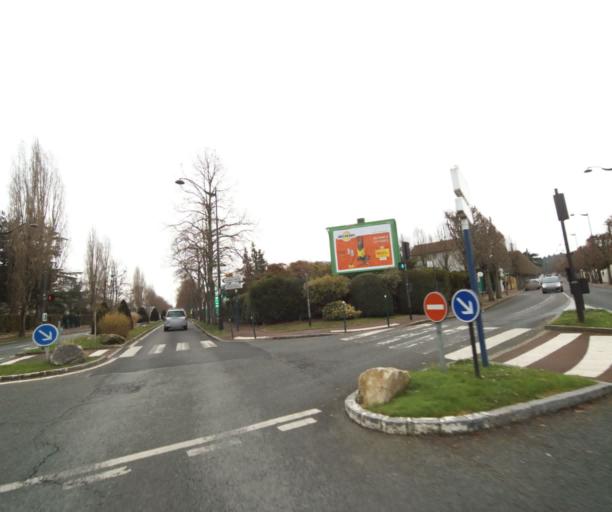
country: FR
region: Ile-de-France
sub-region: Departement des Hauts-de-Seine
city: Rueil-Malmaison
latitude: 48.8623
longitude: 2.1836
